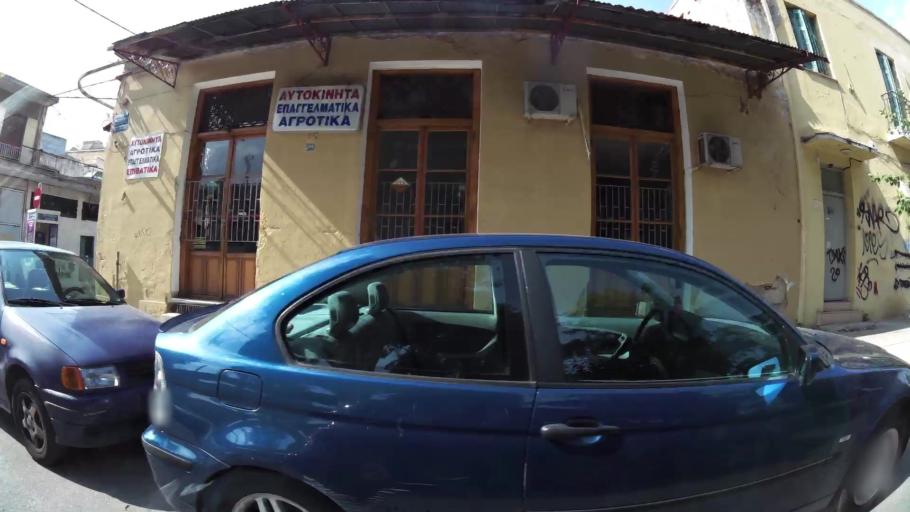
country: GR
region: Attica
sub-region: Nomarchia Athinas
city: Athens
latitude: 37.9933
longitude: 23.7198
